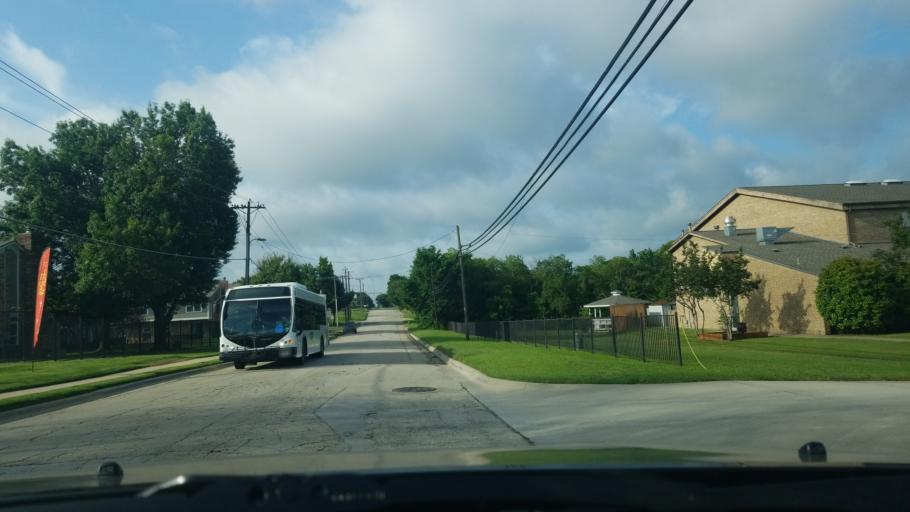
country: US
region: Texas
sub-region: Denton County
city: Denton
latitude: 33.2003
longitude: -97.1417
